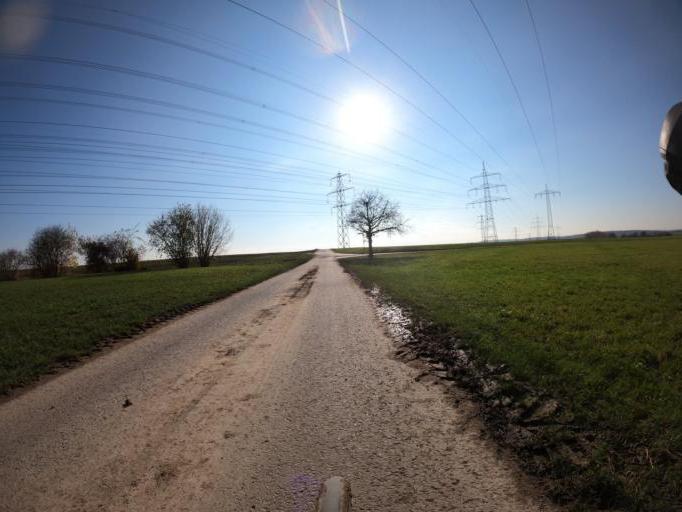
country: DE
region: Baden-Wuerttemberg
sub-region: Regierungsbezirk Stuttgart
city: Magstadt
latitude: 48.7135
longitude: 8.9439
